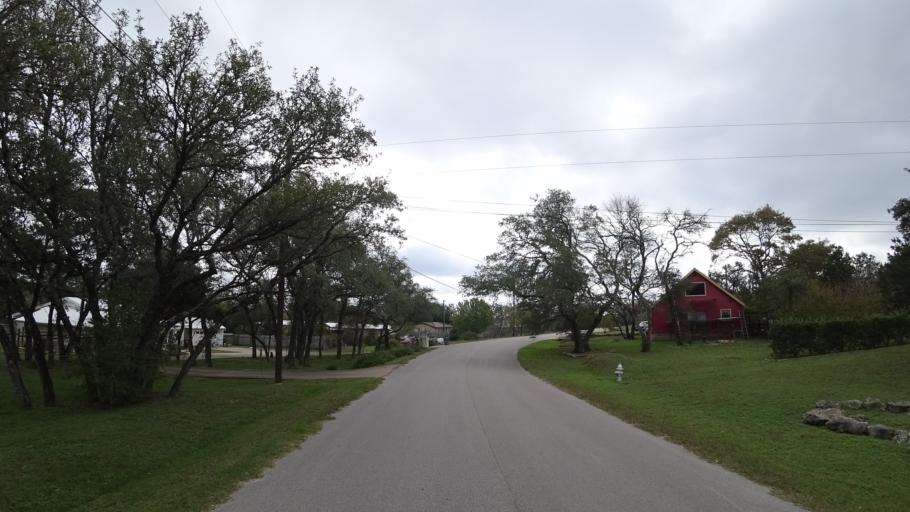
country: US
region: Texas
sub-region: Travis County
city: Barton Creek
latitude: 30.2527
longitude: -97.9206
